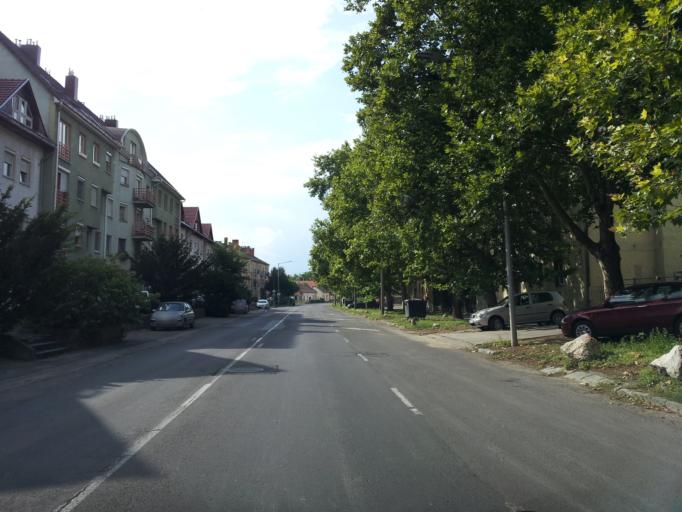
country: HU
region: Pest
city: Vac
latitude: 47.7811
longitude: 19.1287
